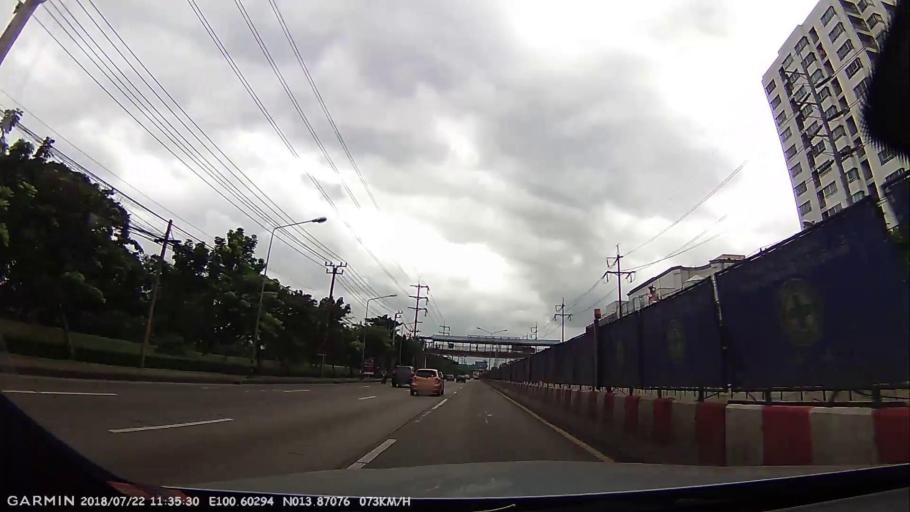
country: TH
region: Bangkok
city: Bang Khen
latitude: 13.8708
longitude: 100.6029
